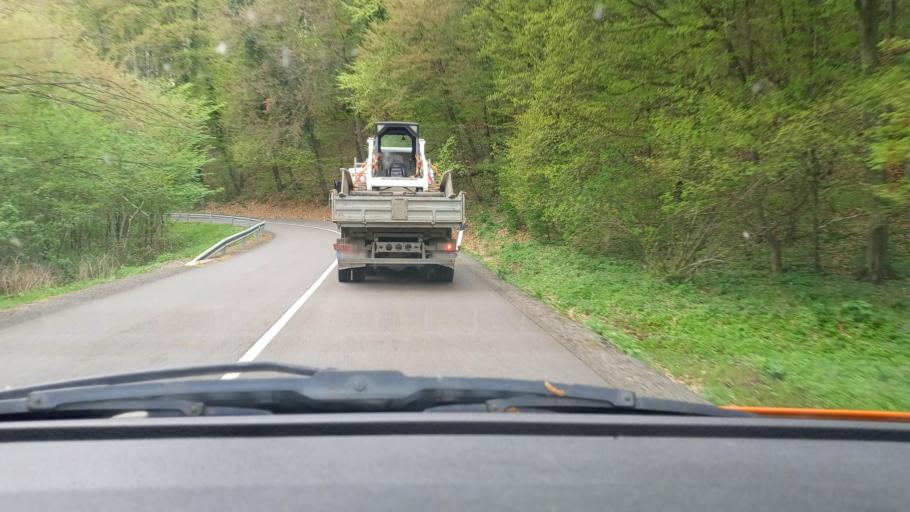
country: HU
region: Baranya
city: Komlo
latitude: 46.2070
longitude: 18.3004
